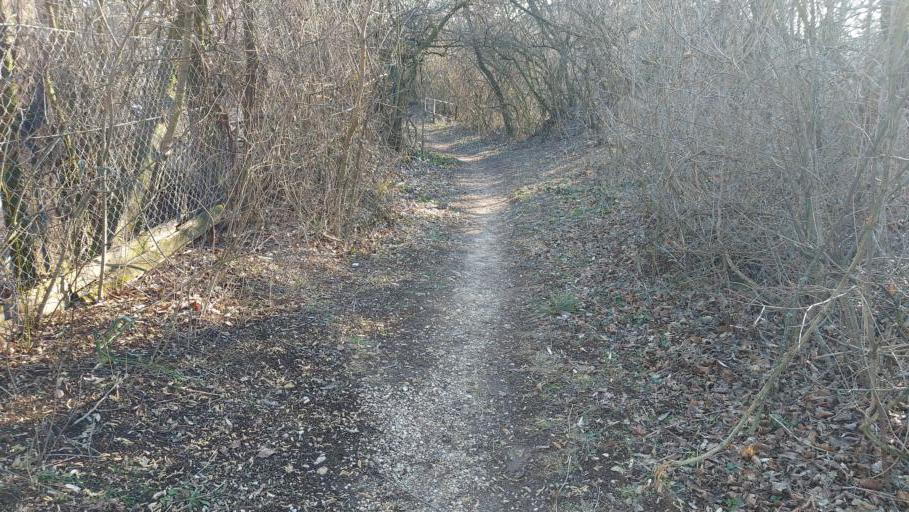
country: HU
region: Pest
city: Budaors
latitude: 47.4706
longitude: 18.9372
